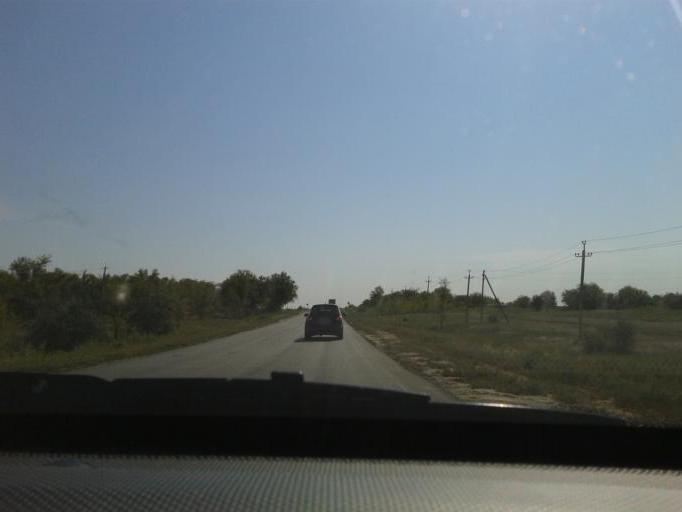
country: RU
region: Volgograd
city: Leninsk
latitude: 48.6969
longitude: 45.2664
